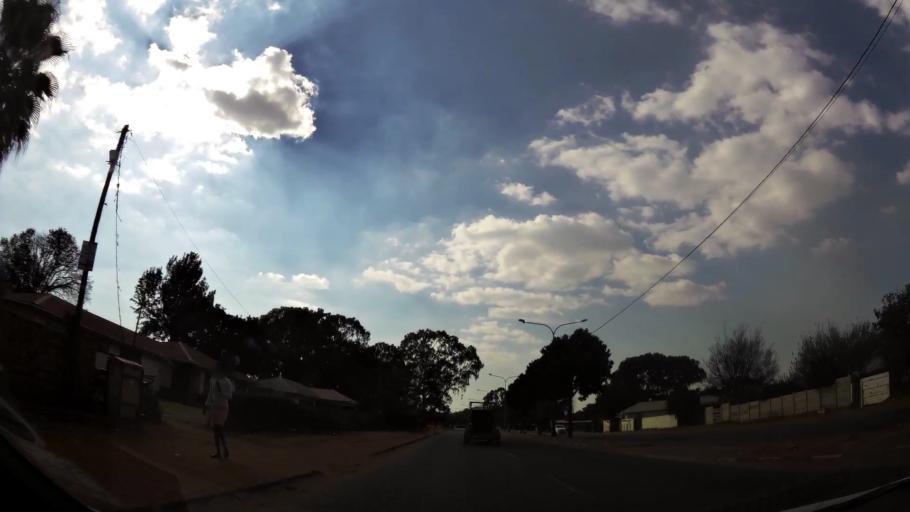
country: ZA
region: Gauteng
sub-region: Ekurhuleni Metropolitan Municipality
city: Germiston
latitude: -26.1928
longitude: 28.1621
